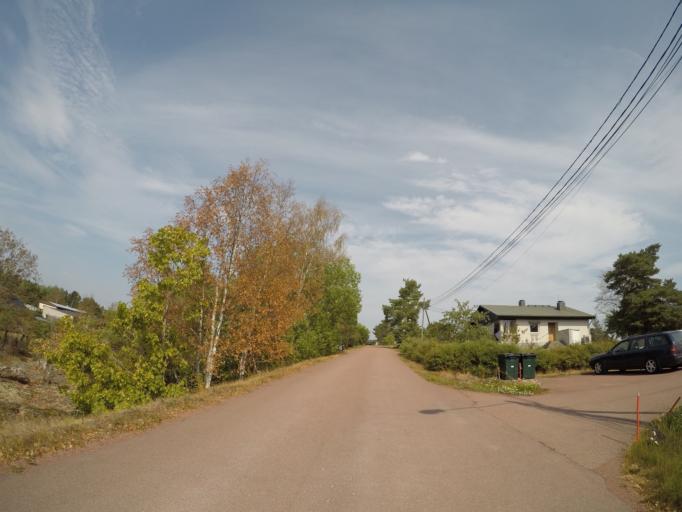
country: AX
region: Alands landsbygd
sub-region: Finstroem
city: Finstroem
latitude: 60.2343
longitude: 19.9888
